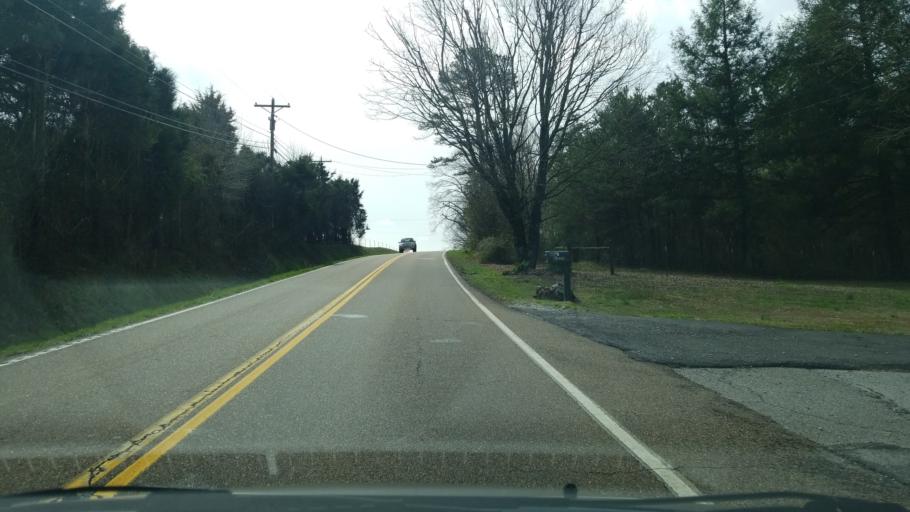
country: US
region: Tennessee
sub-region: Hamilton County
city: Collegedale
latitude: 35.1093
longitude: -85.0662
